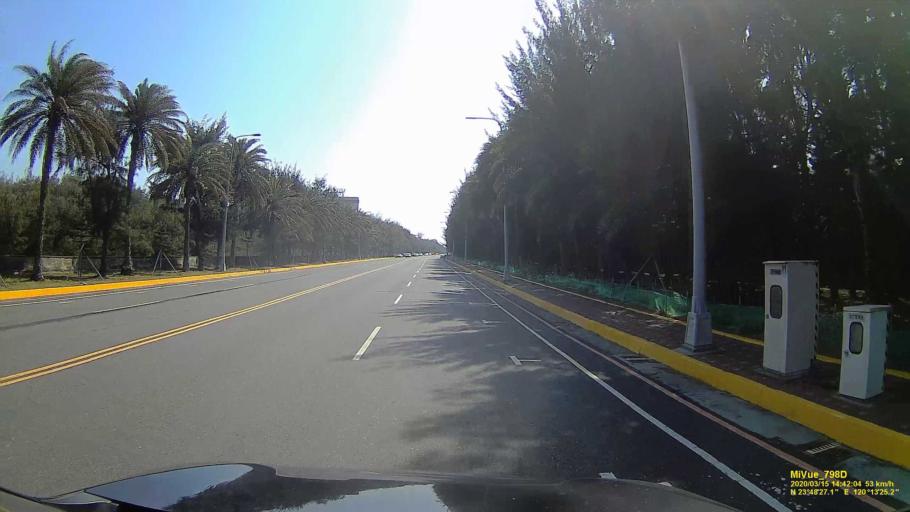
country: TW
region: Taiwan
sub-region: Yunlin
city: Douliu
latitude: 23.8073
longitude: 120.2235
